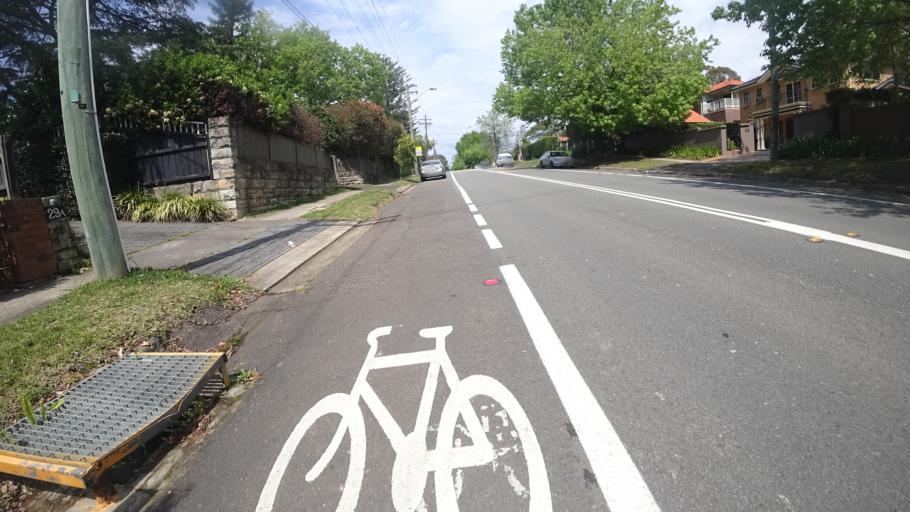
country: AU
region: New South Wales
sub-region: City of Sydney
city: Pymble
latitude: -33.7356
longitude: 151.1374
